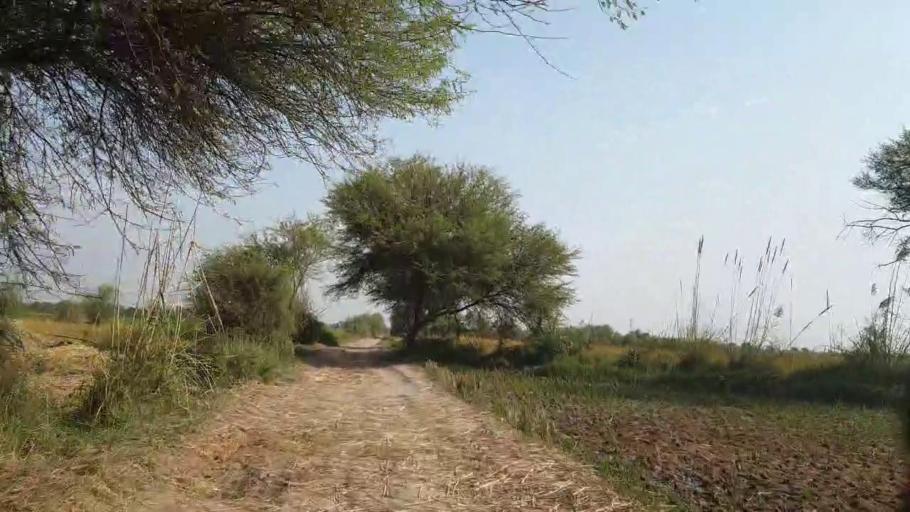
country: PK
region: Sindh
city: Tando Muhammad Khan
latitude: 25.0595
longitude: 68.4253
